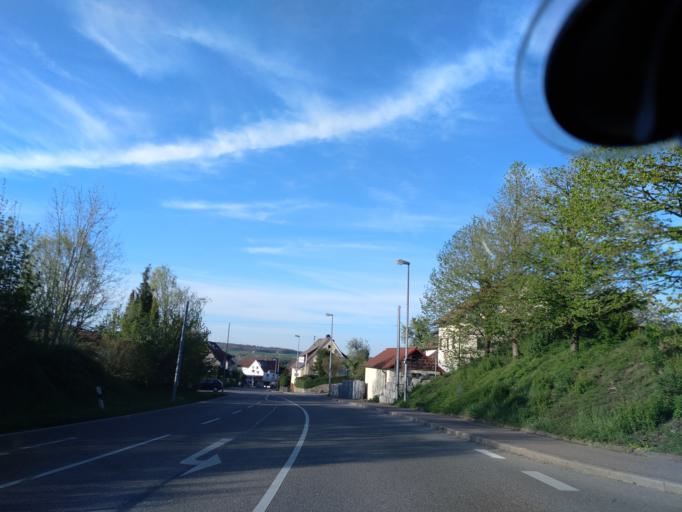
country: DE
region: Baden-Wuerttemberg
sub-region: Regierungsbezirk Stuttgart
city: Kirchberg an der Jagst
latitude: 49.1995
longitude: 9.9813
